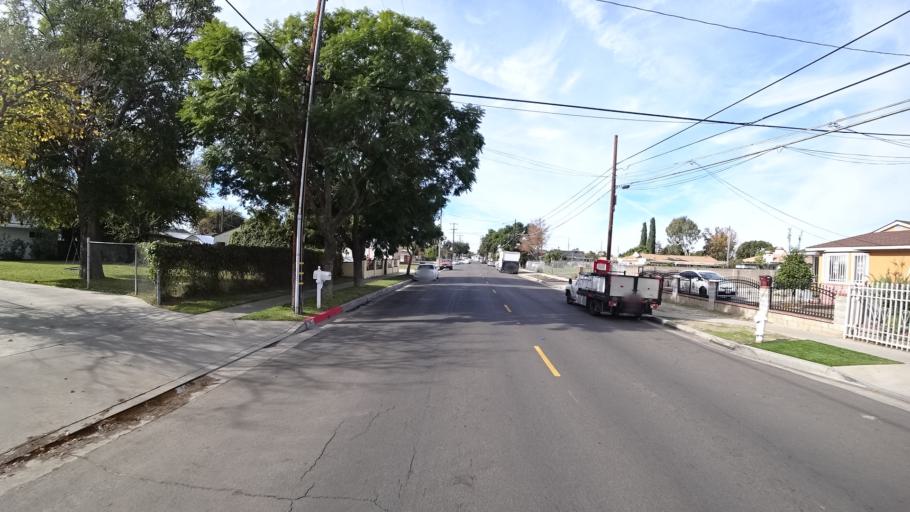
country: US
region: California
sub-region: Orange County
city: Garden Grove
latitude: 33.7488
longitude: -117.9348
